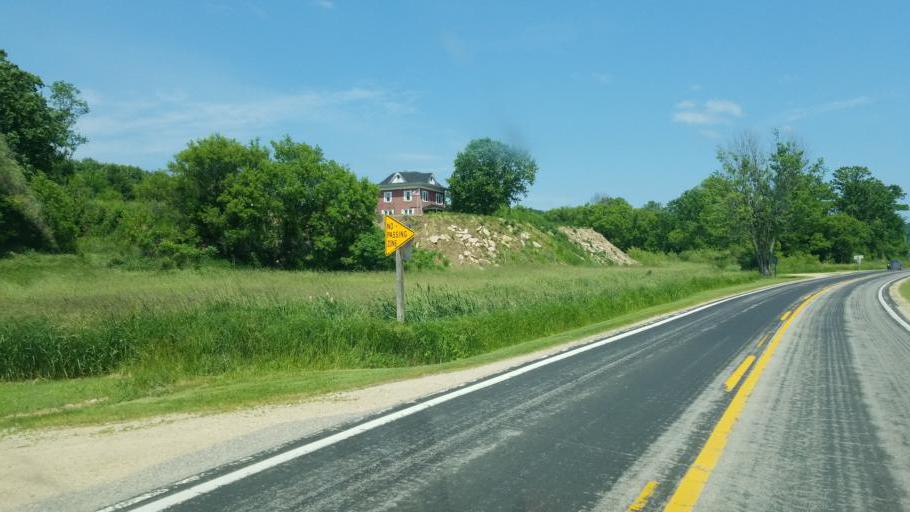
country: US
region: Wisconsin
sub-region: Monroe County
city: Cashton
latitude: 43.5743
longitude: -90.6295
